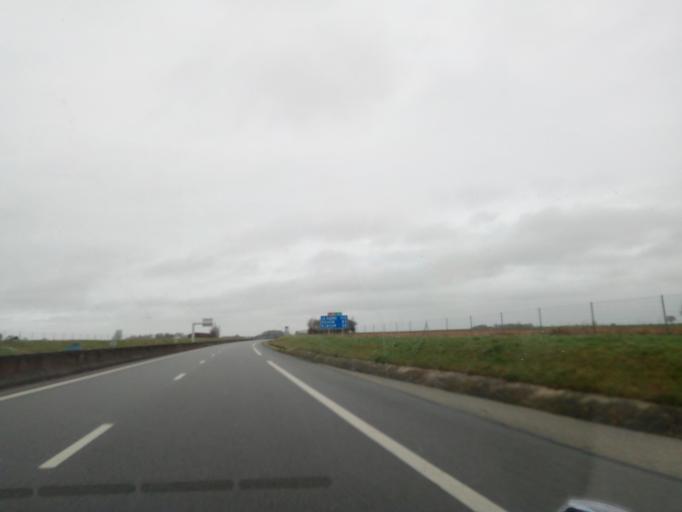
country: FR
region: Lower Normandy
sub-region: Departement du Calvados
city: Orbec
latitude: 49.0392
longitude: 0.4448
